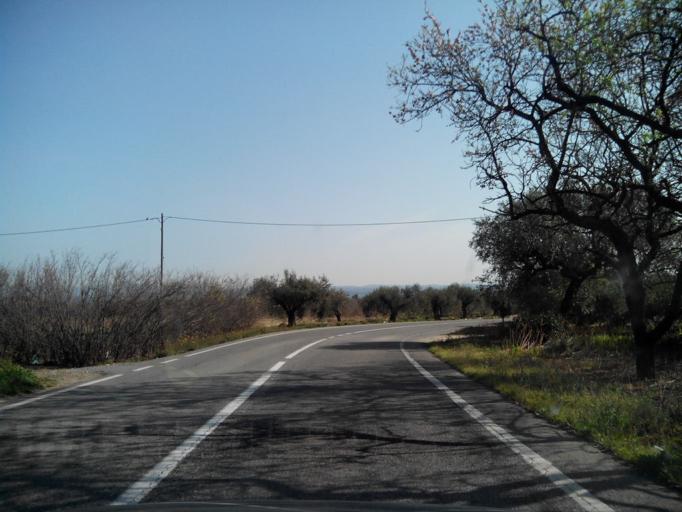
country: ES
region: Catalonia
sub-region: Provincia de Tarragona
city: La Selva
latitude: 41.2146
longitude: 1.1556
